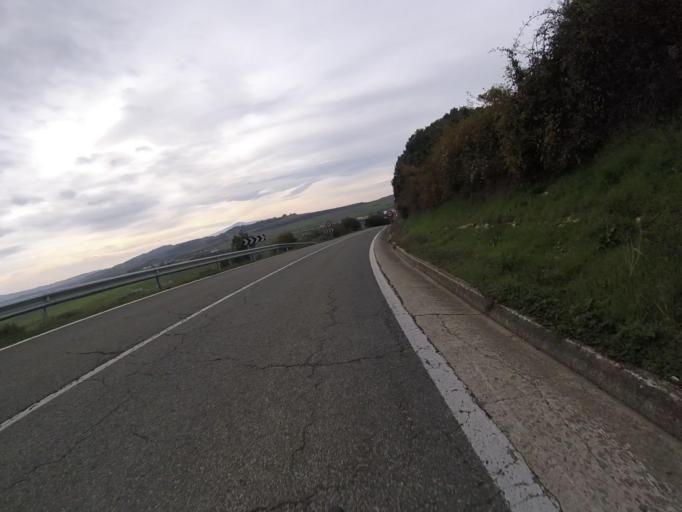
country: ES
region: Navarre
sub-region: Provincia de Navarra
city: Lezaun
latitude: 42.7293
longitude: -2.0160
